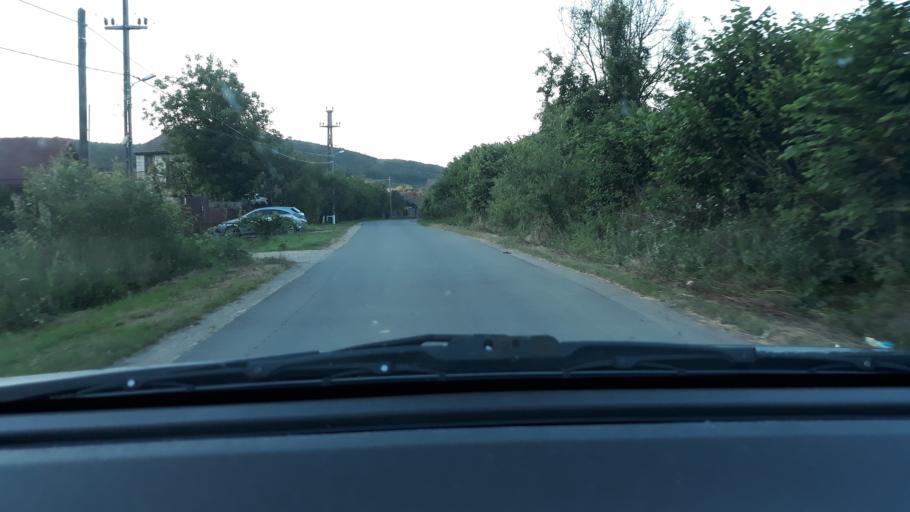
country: RO
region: Bihor
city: Hidiselu de Sus
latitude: 46.9419
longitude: 22.0197
